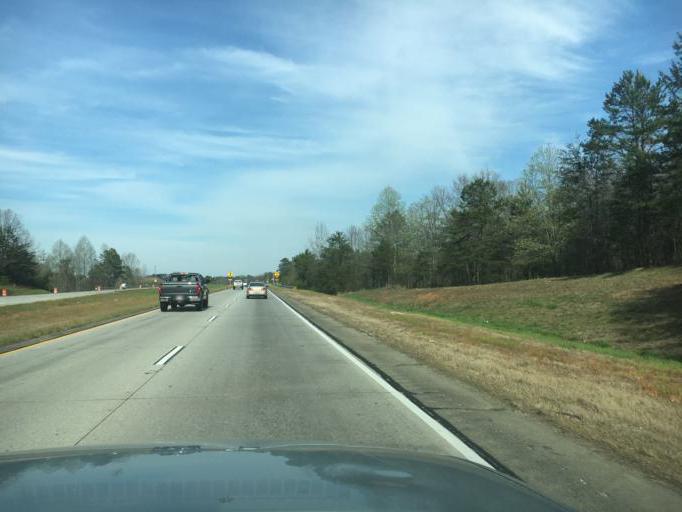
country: US
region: Georgia
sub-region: Hall County
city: Gainesville
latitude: 34.3475
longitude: -83.7641
